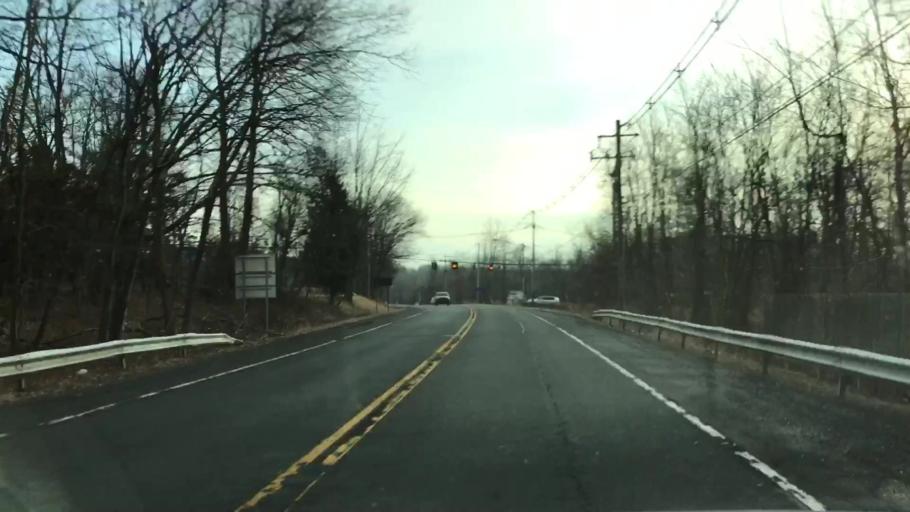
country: US
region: New York
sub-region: Rockland County
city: Pomona
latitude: 41.1823
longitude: -74.0560
